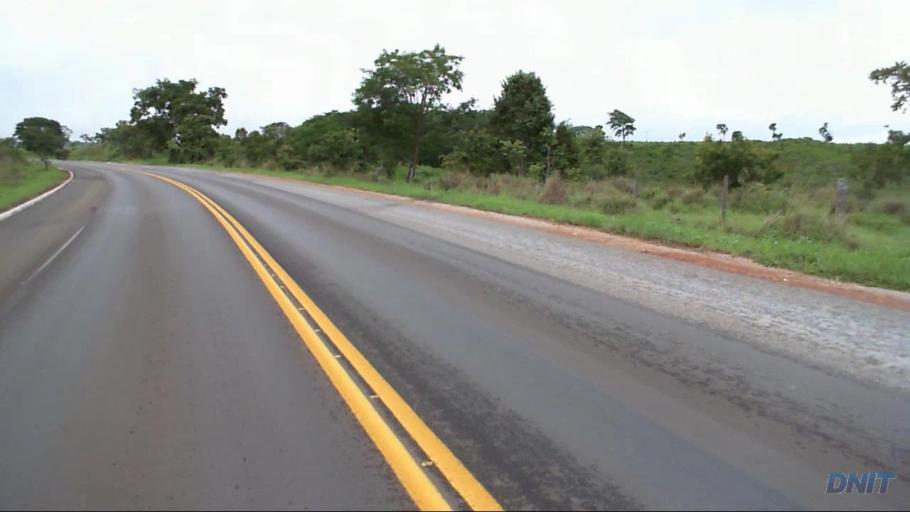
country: BR
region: Goias
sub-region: Padre Bernardo
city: Padre Bernardo
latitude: -15.1797
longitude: -48.4246
